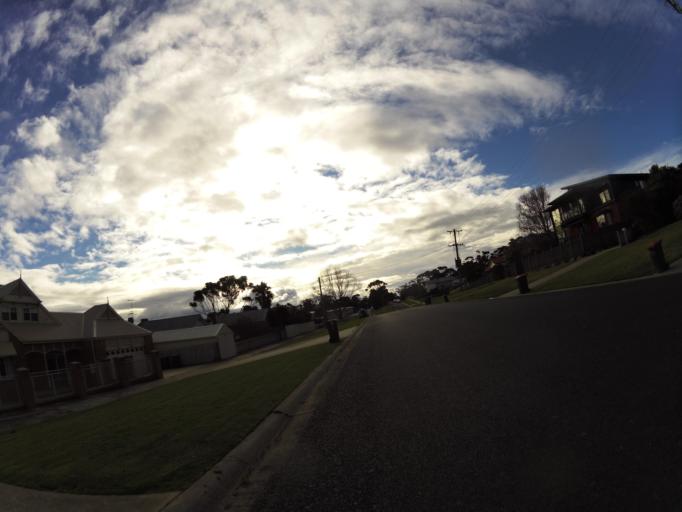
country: AU
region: Victoria
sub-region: Bass Coast
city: North Wonthaggi
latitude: -38.6101
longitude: 145.5889
